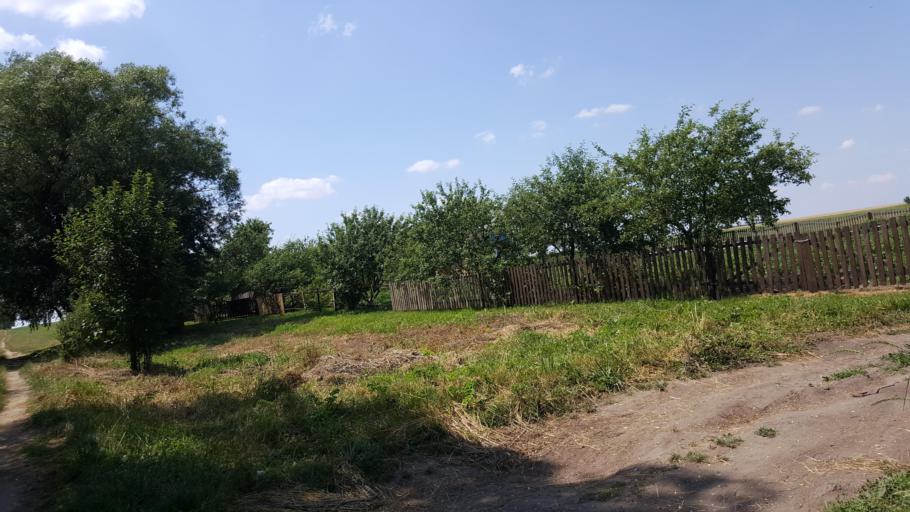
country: BY
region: Brest
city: Kamyanyets
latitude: 52.4052
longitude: 23.7807
